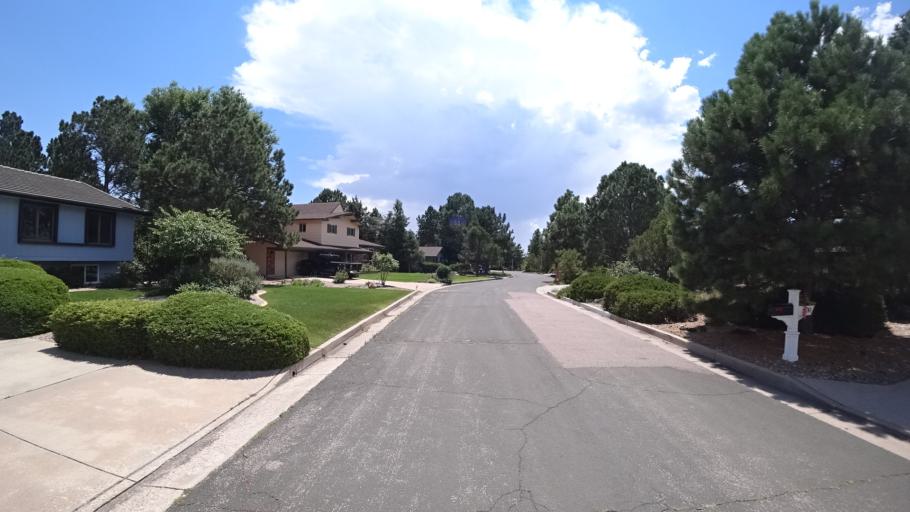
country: US
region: Colorado
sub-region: El Paso County
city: Air Force Academy
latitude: 38.9337
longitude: -104.8275
